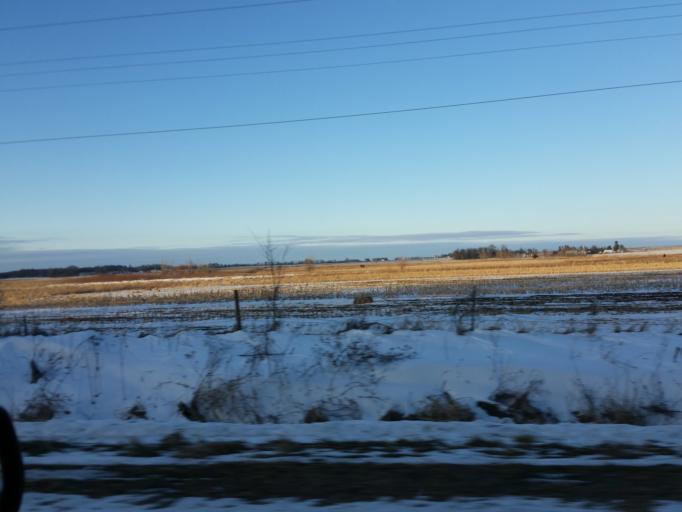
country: US
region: Iowa
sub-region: Butler County
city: Allison
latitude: 42.7447
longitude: -92.9092
